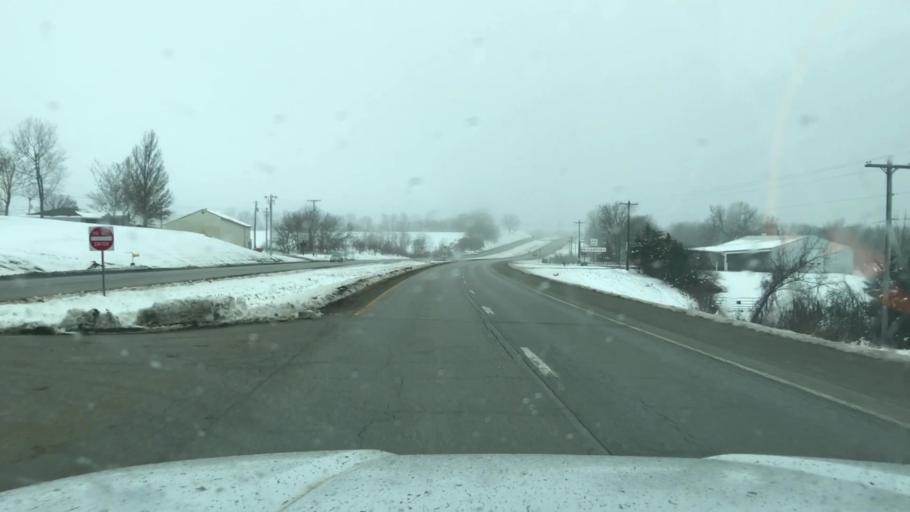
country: US
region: Missouri
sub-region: Andrew County
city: Country Club Village
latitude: 39.8668
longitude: -94.8084
